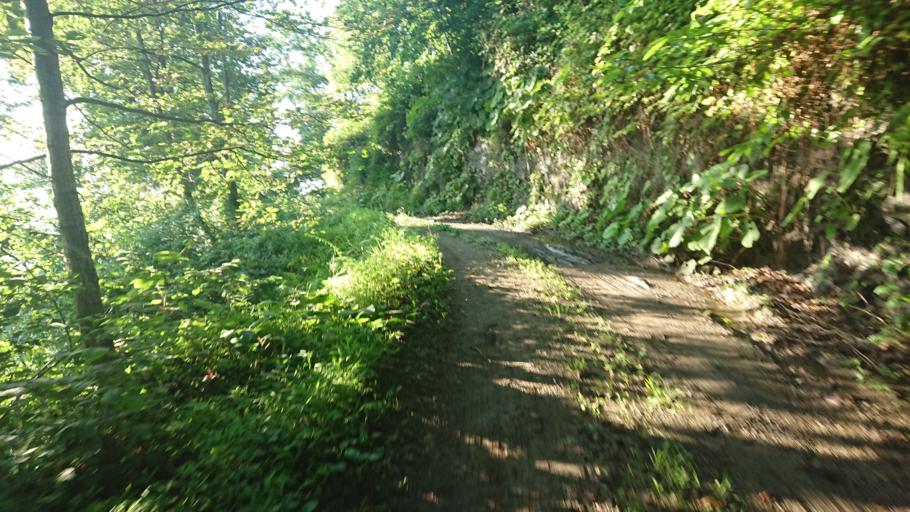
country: TR
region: Rize
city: Rize
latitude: 40.9762
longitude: 40.4987
